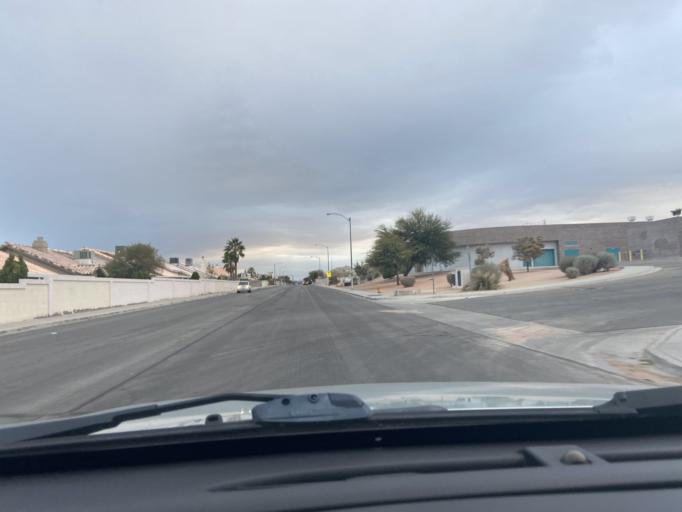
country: US
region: Nevada
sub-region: Clark County
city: Las Vegas
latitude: 36.2302
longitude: -115.1847
